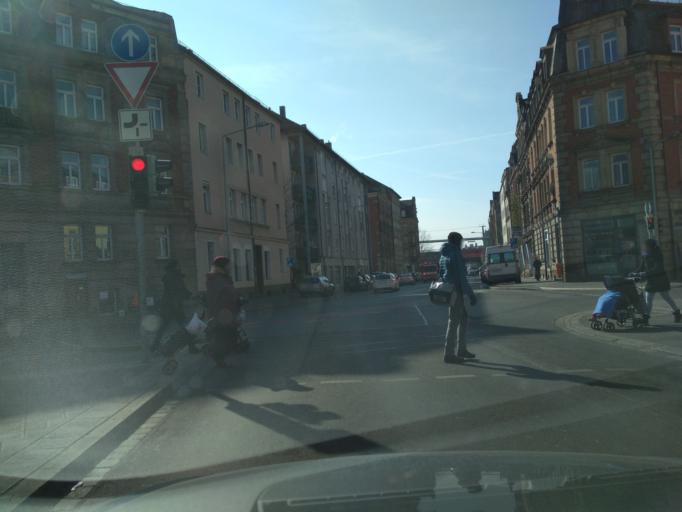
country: DE
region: Bavaria
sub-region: Regierungsbezirk Mittelfranken
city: Nuernberg
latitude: 49.4470
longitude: 11.0575
